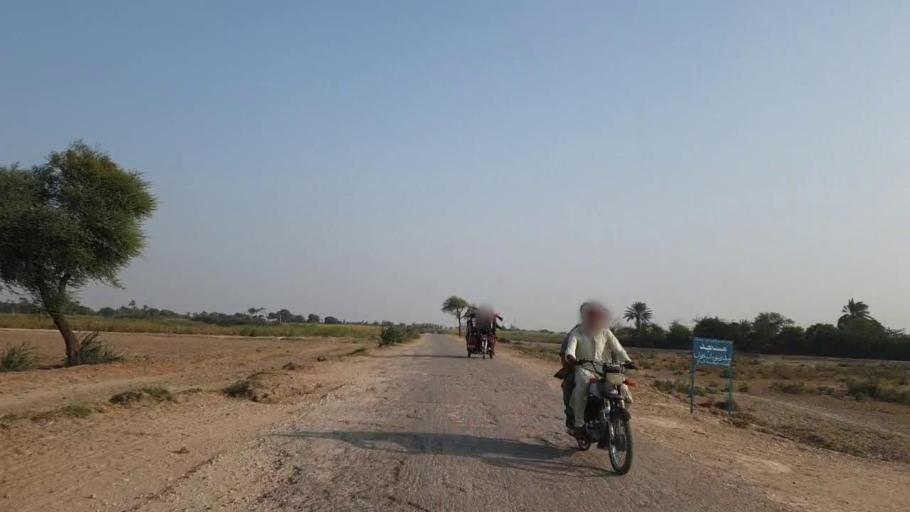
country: PK
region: Sindh
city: Bulri
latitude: 24.9720
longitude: 68.4038
